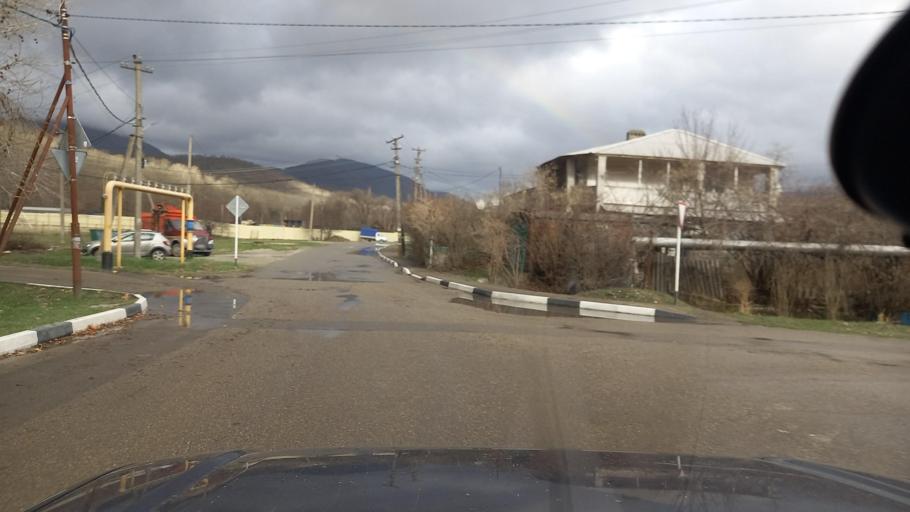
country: RU
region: Krasnodarskiy
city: Pshada
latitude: 44.4766
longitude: 38.3994
